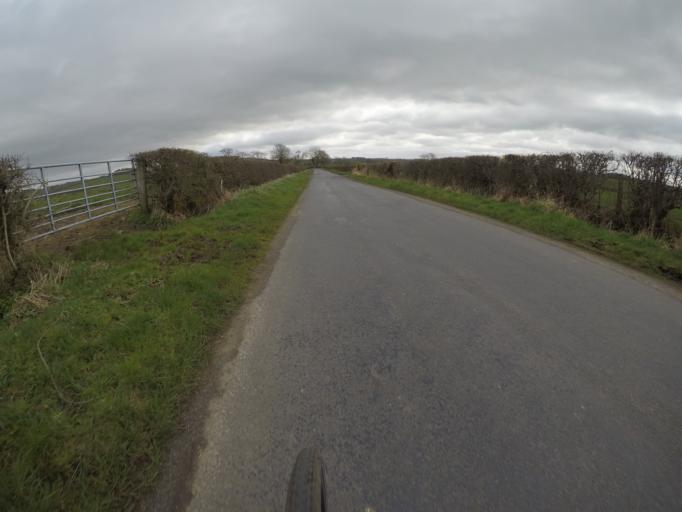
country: GB
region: Scotland
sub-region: East Ayrshire
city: Stewarton
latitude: 55.6722
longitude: -4.5602
